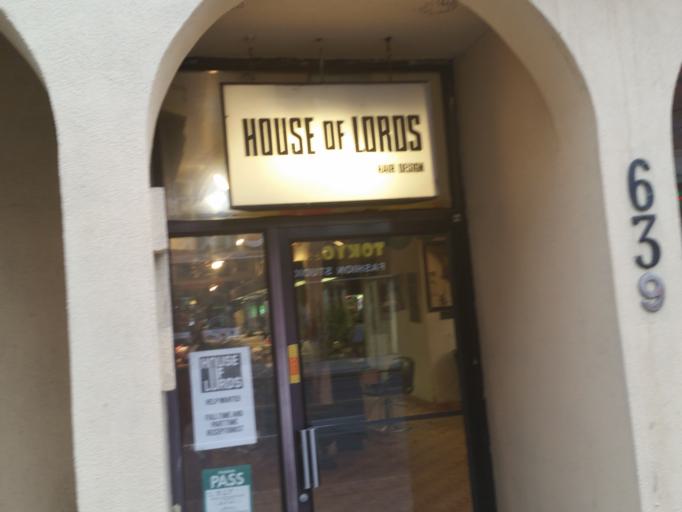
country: CA
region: Ontario
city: Toronto
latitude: 43.6676
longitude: -79.3858
